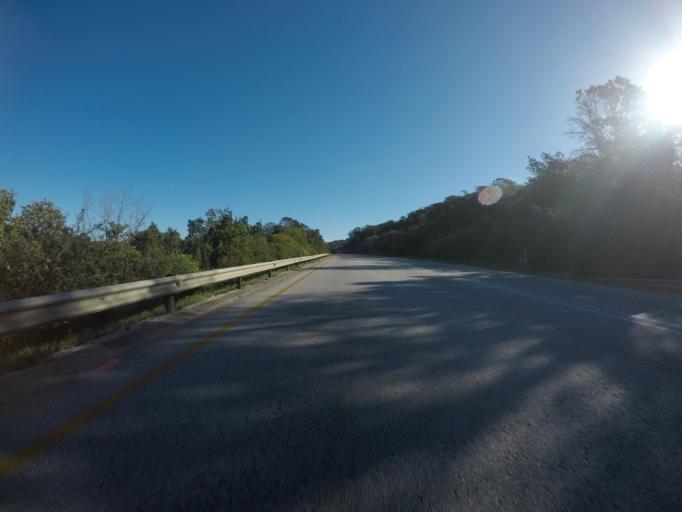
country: ZA
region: Eastern Cape
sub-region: Cacadu District Municipality
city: Jeffrey's Bay
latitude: -33.9025
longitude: 25.0837
